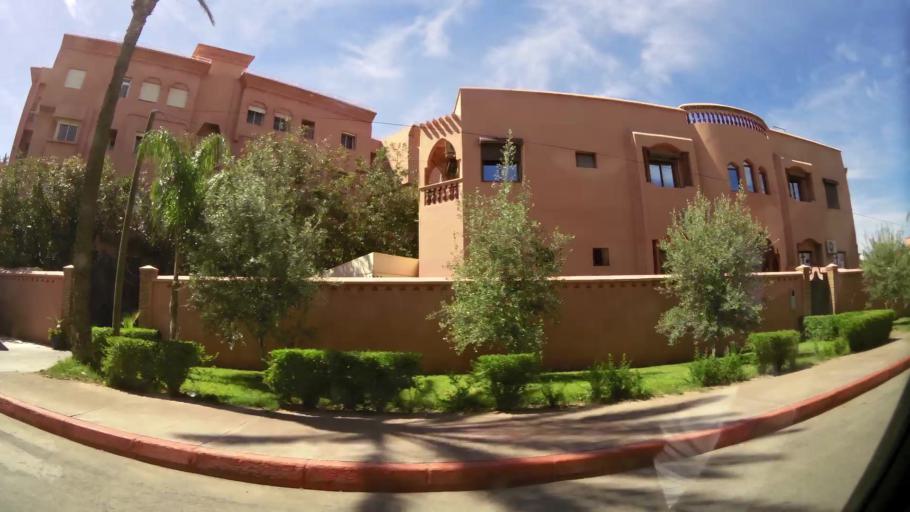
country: MA
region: Marrakech-Tensift-Al Haouz
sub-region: Marrakech
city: Marrakesh
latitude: 31.6730
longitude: -8.0032
